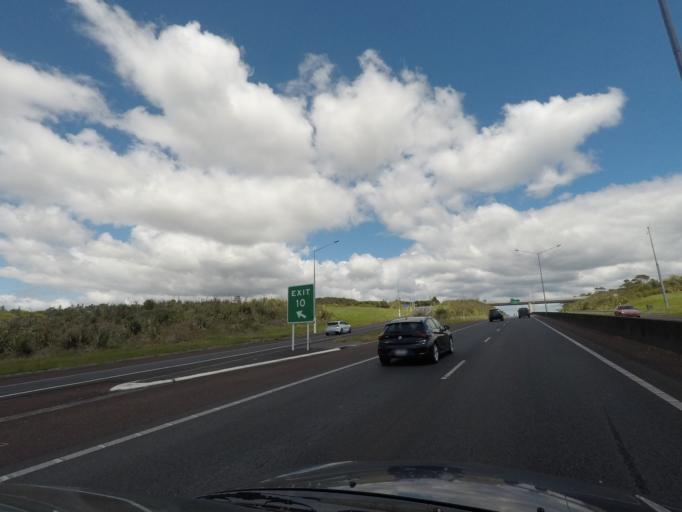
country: NZ
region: Auckland
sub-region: Auckland
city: Rosebank
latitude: -36.8082
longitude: 174.6218
